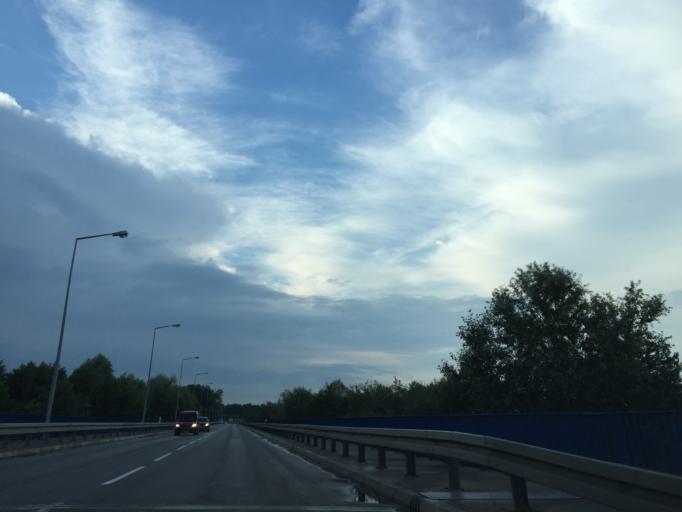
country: PL
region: Masovian Voivodeship
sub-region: Powiat ostrowski
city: Brok
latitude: 52.6927
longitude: 21.8509
